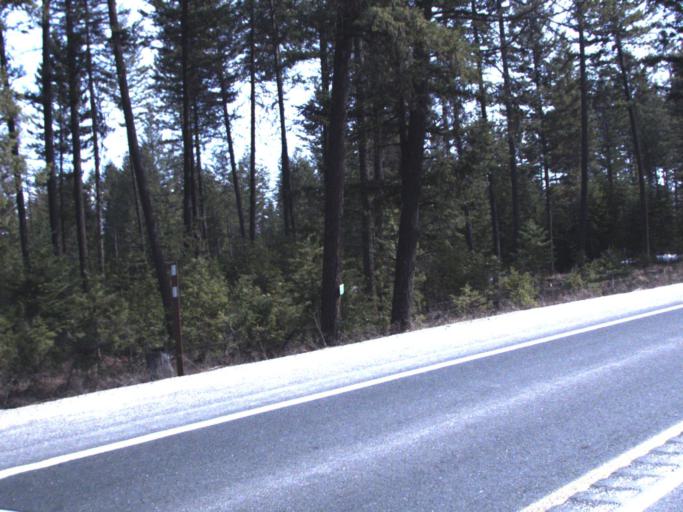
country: US
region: Washington
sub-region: Stevens County
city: Colville
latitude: 48.5204
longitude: -117.6897
